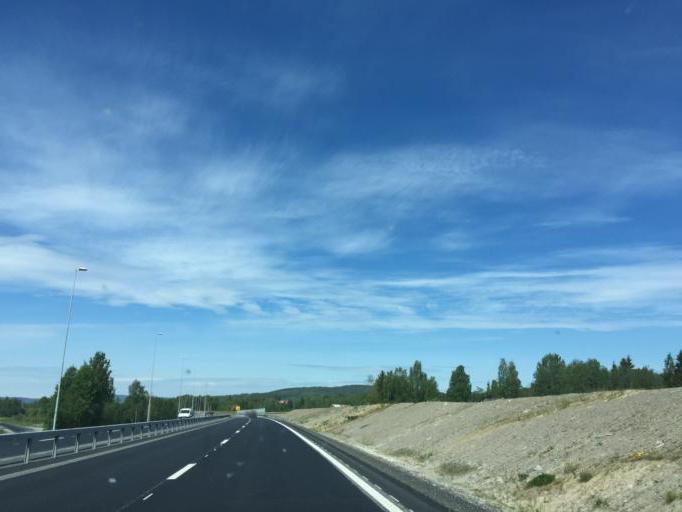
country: NO
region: Hedmark
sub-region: Kongsvinger
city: Spetalen
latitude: 60.2295
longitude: 11.8512
